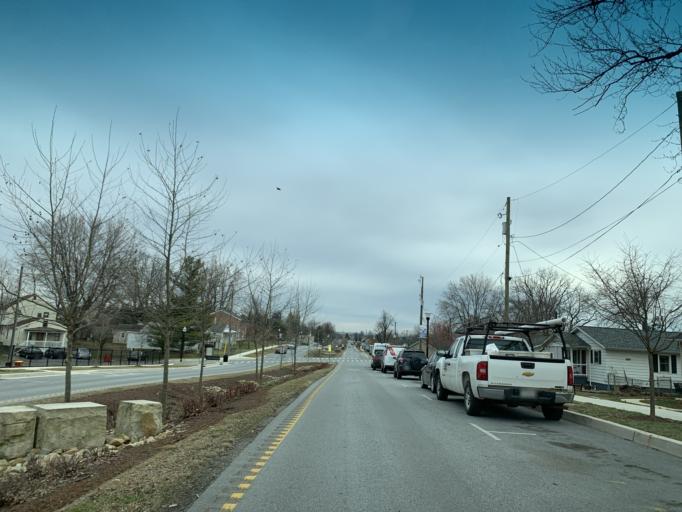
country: US
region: West Virginia
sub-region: Jefferson County
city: Ranson
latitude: 39.3048
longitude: -77.8564
